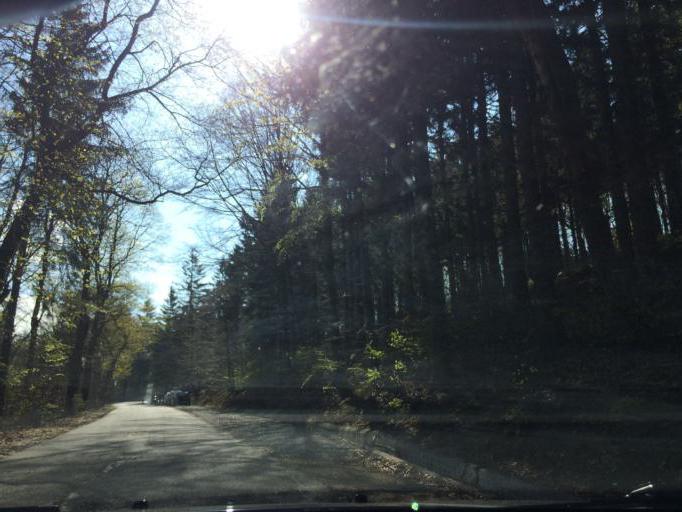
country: PL
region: Lower Silesian Voivodeship
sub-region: Powiat klodzki
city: Jugow
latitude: 50.6580
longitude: 16.5236
